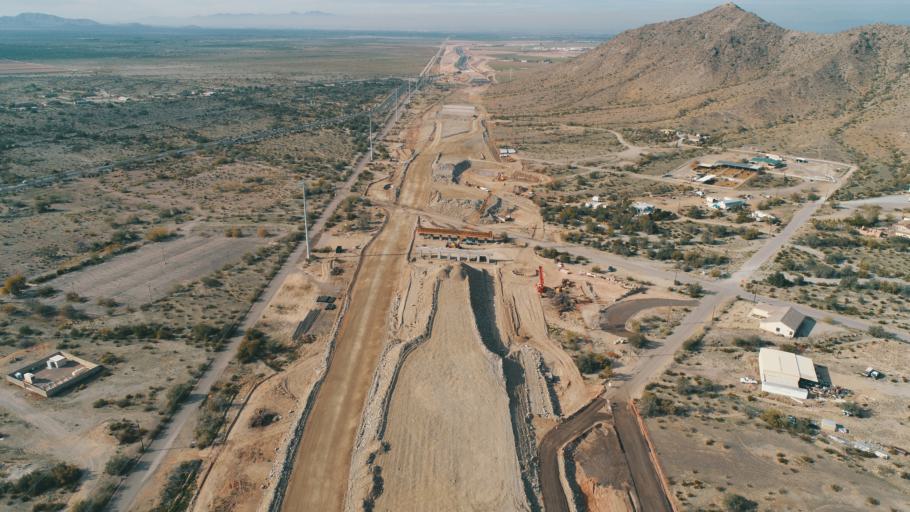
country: US
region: Arizona
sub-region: Maricopa County
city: Laveen
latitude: 33.3130
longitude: -112.1552
